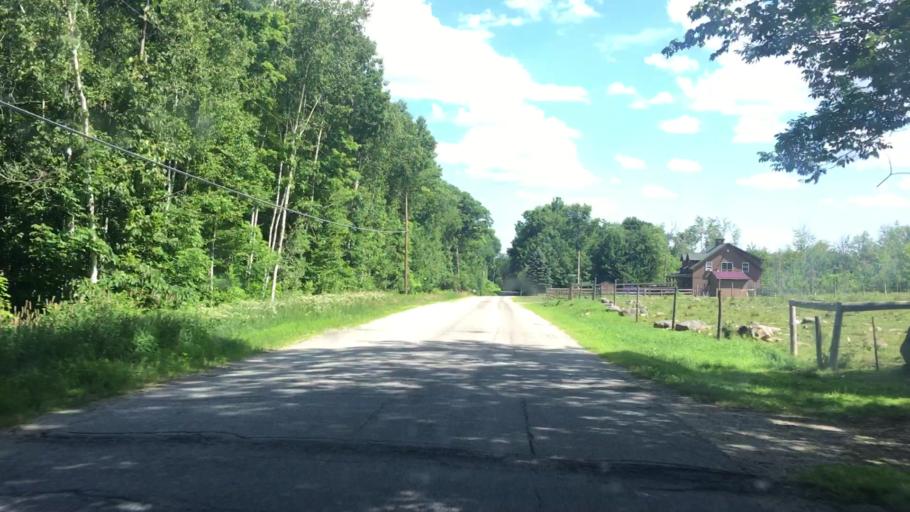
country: US
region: Maine
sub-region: Franklin County
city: Chesterville
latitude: 44.5667
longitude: -70.1447
